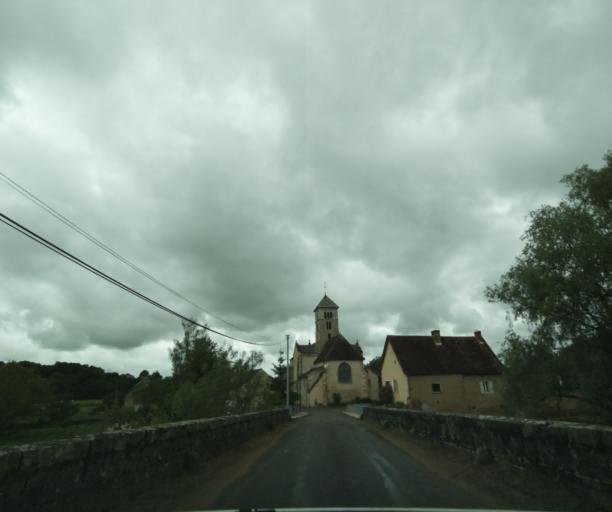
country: FR
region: Bourgogne
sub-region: Departement de Saone-et-Loire
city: Charolles
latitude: 46.4715
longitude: 4.3364
